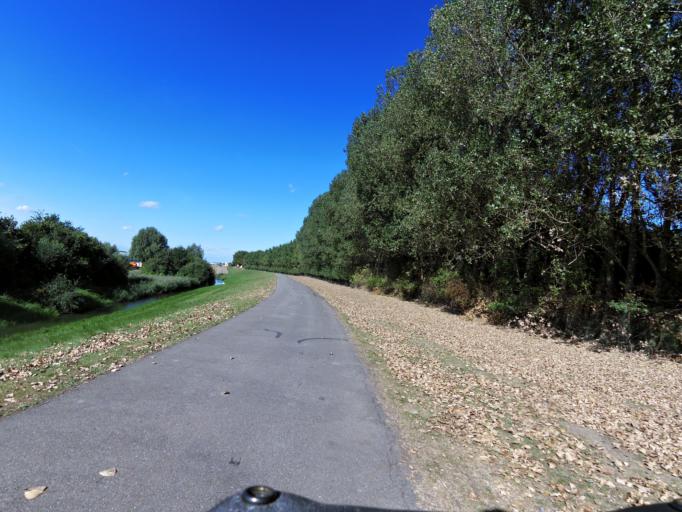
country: NL
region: South Holland
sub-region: Gemeente Zwijndrecht
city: Zwijndrecht
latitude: 51.7904
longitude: 4.6184
